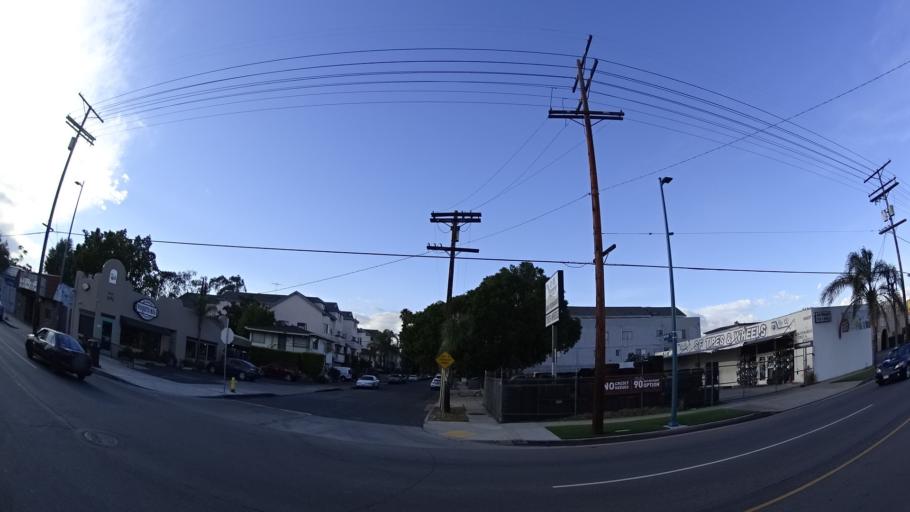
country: US
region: California
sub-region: Los Angeles County
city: North Hollywood
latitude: 34.1649
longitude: -118.3632
